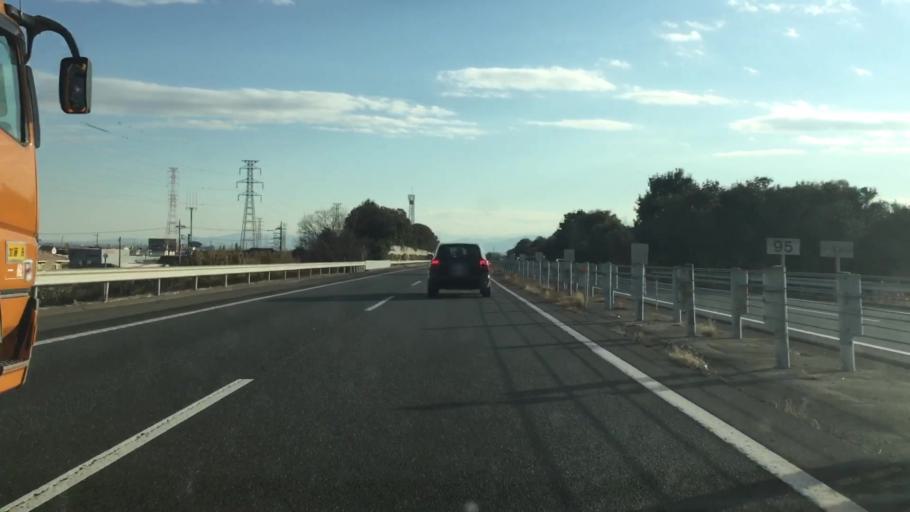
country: JP
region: Gunma
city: Kanekomachi
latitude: 36.4000
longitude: 139.0248
